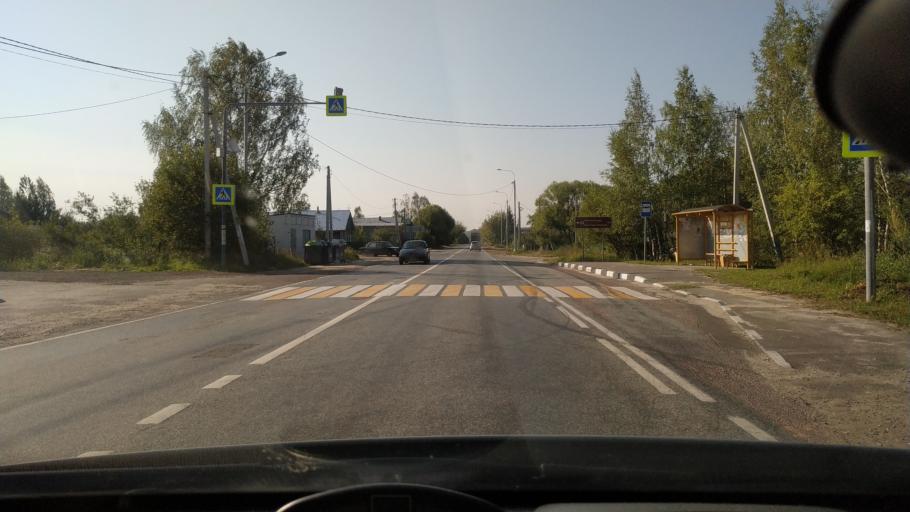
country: RU
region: Moskovskaya
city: Tugolesskiy Bor
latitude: 55.5257
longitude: 39.7106
